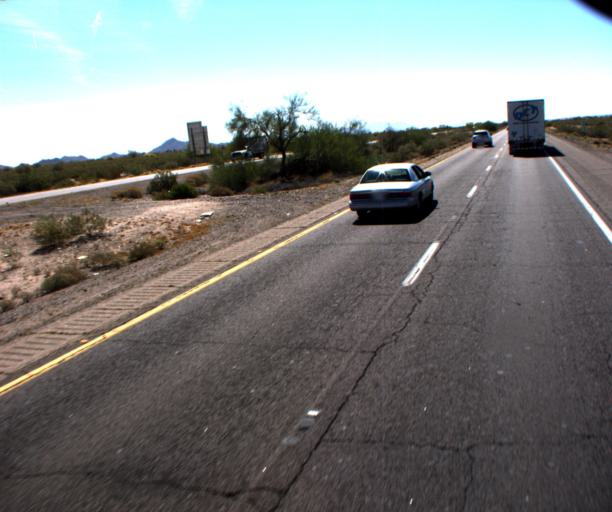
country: US
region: Arizona
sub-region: Pinal County
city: Sacaton
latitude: 32.9949
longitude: -111.7466
